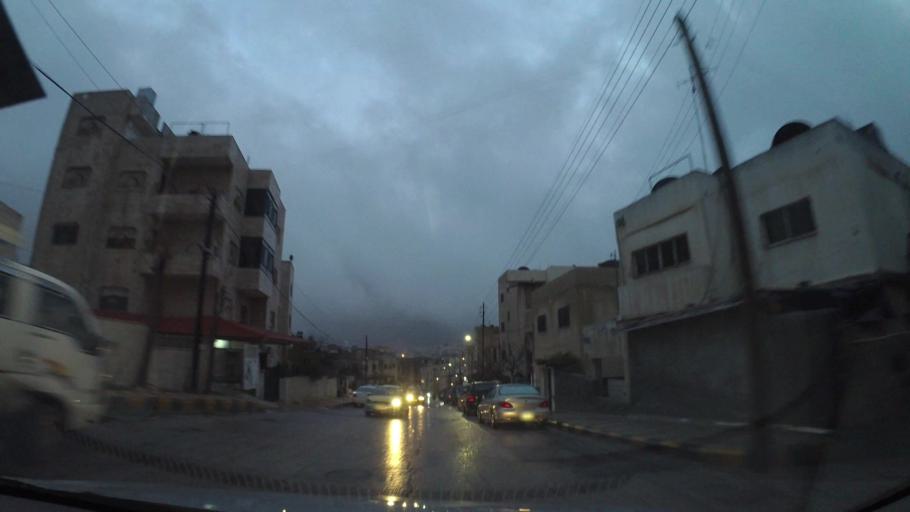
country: JO
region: Amman
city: Al Jubayhah
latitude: 32.0275
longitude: 35.8481
